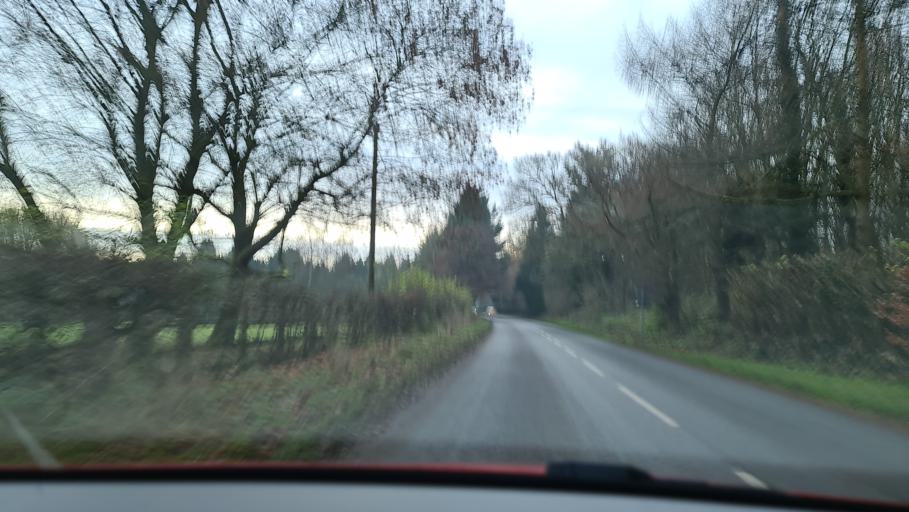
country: GB
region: England
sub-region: Buckinghamshire
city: Great Missenden
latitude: 51.7090
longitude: -0.7227
